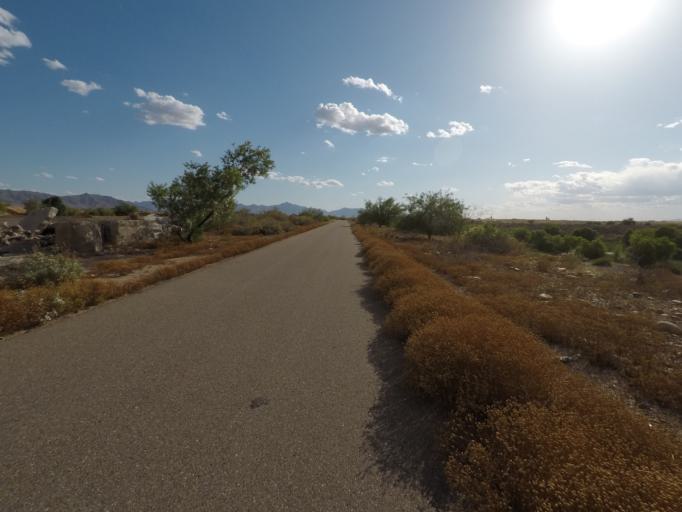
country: US
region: Arizona
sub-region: Maricopa County
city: Phoenix
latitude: 33.4163
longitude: -112.0849
